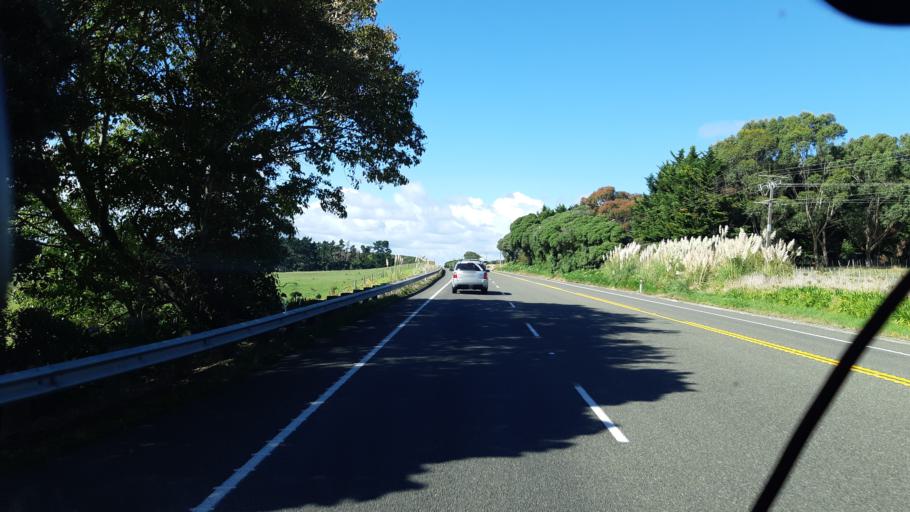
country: NZ
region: Manawatu-Wanganui
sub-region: Wanganui District
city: Wanganui
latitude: -39.9730
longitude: 175.1139
